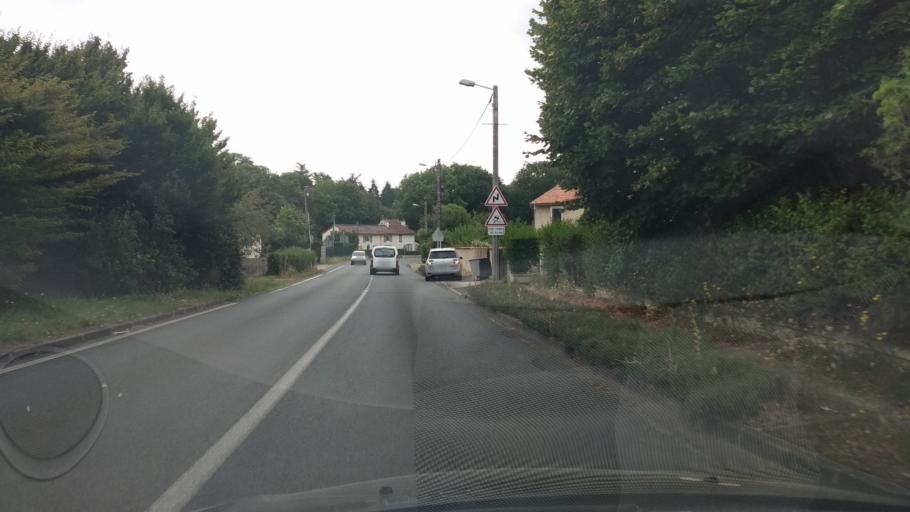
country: FR
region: Poitou-Charentes
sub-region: Departement de la Vienne
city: Saint-Benoit
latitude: 46.5587
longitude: 0.3551
